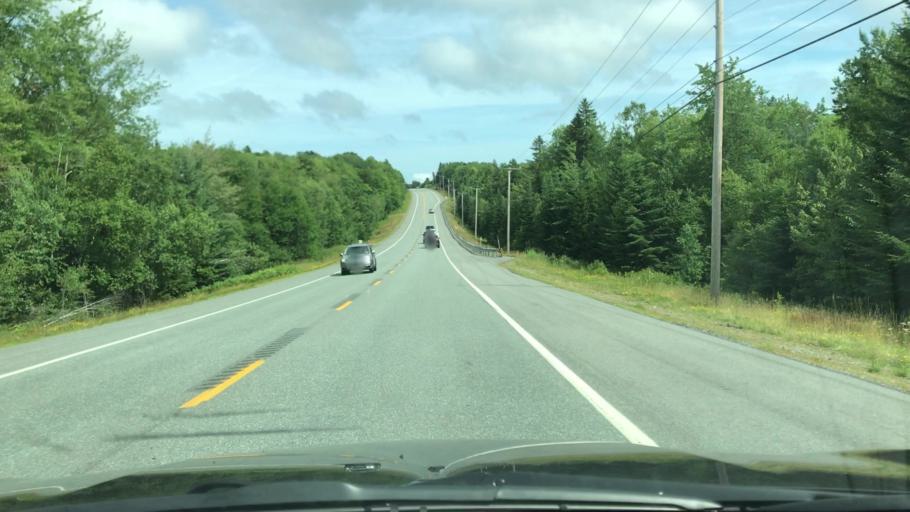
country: US
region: Maine
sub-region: Hancock County
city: Surry
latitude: 44.5500
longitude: -68.5293
